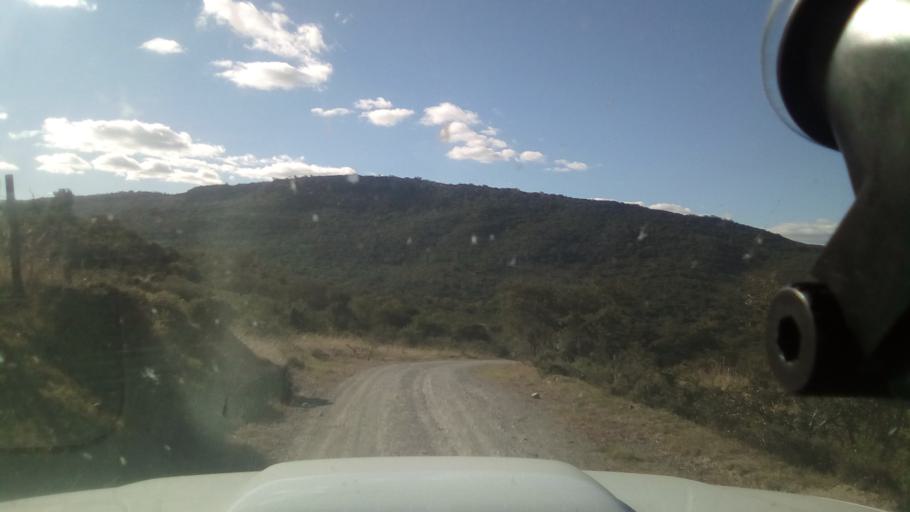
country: ZA
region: Eastern Cape
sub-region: Buffalo City Metropolitan Municipality
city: Bhisho
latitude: -32.7307
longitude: 27.3483
